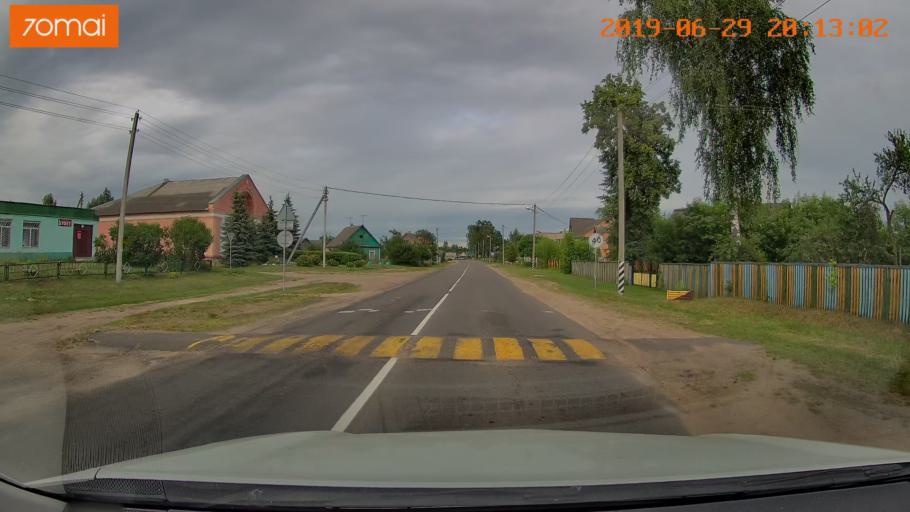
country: BY
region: Brest
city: Lahishyn
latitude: 52.3652
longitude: 26.1424
